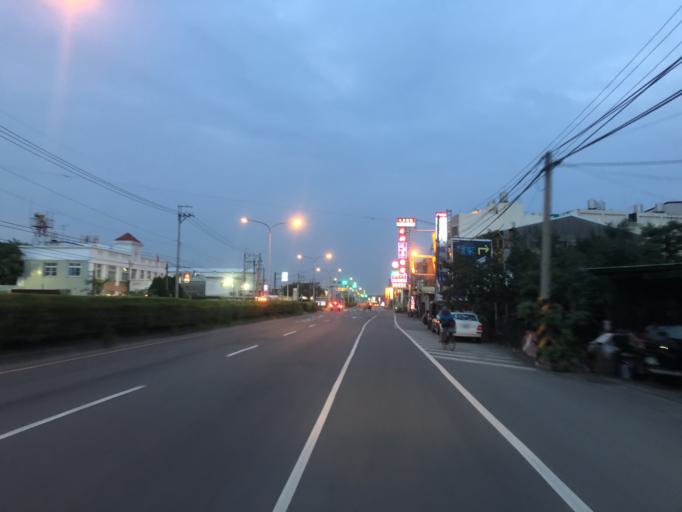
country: TW
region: Taiwan
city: Yujing
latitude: 23.1359
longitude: 120.3223
